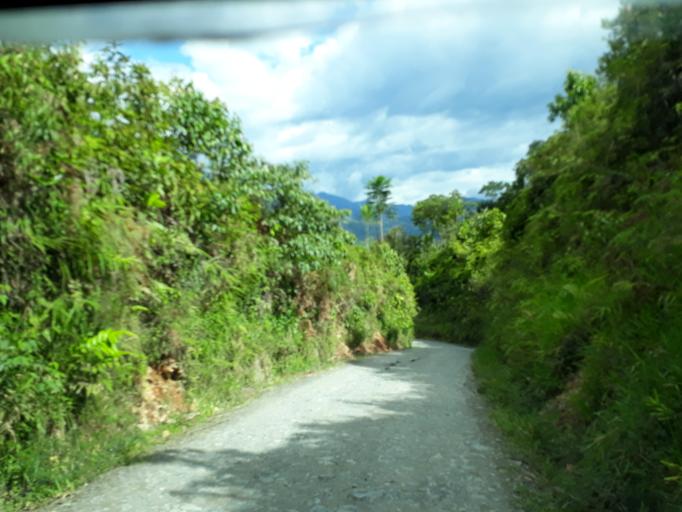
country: CO
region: Cundinamarca
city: Topaipi
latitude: 5.3862
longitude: -74.1955
